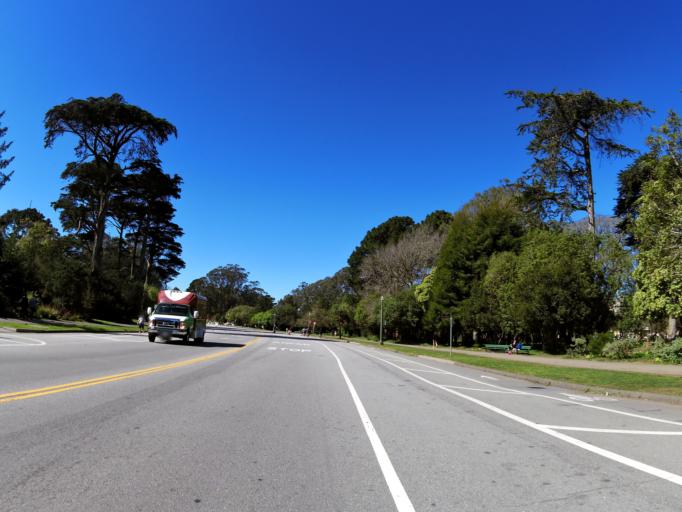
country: US
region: California
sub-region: San Francisco County
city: San Francisco
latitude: 37.7725
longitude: -122.4643
